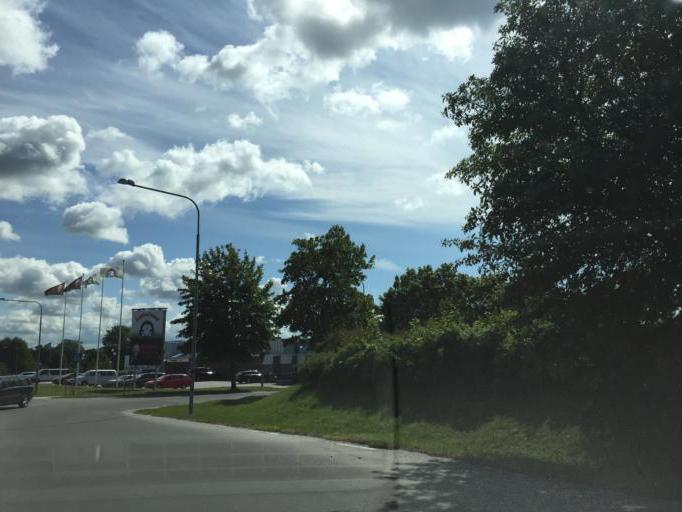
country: SE
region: Gotland
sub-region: Gotland
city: Visby
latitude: 57.6164
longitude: 18.2835
